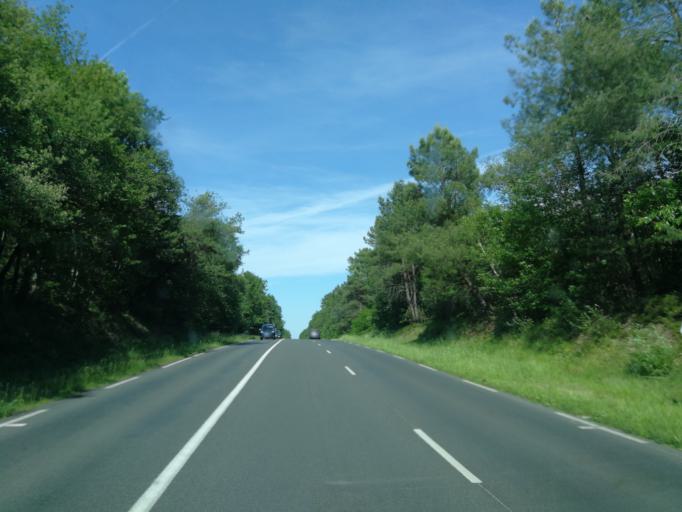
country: FR
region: Centre
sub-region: Departement d'Indre-et-Loire
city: Huismes
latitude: 47.2017
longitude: 0.3240
